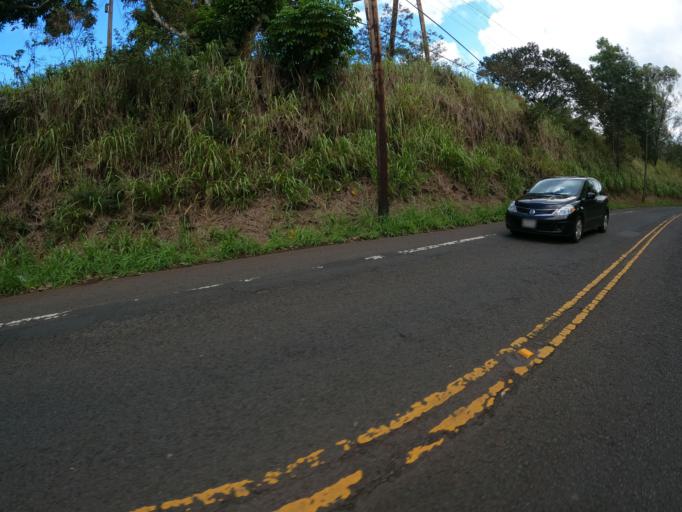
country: US
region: Hawaii
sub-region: Honolulu County
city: Wahiawa
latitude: 21.5028
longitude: -158.0304
